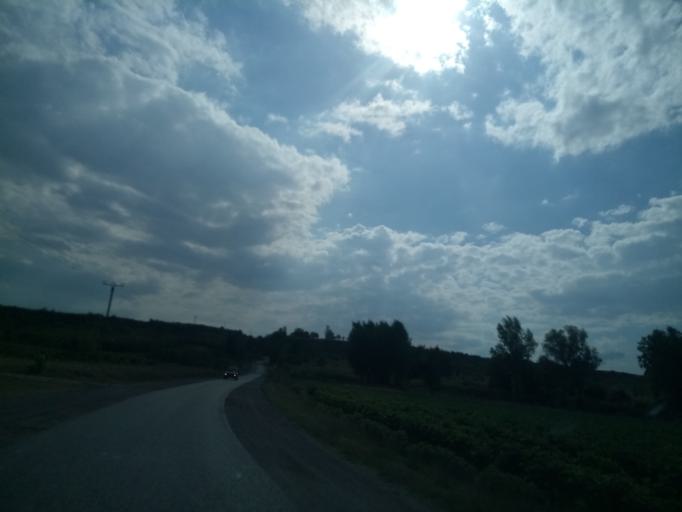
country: RS
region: Autonomna Pokrajina Vojvodina
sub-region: Sremski Okrug
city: Irig
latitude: 45.1043
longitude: 19.9103
